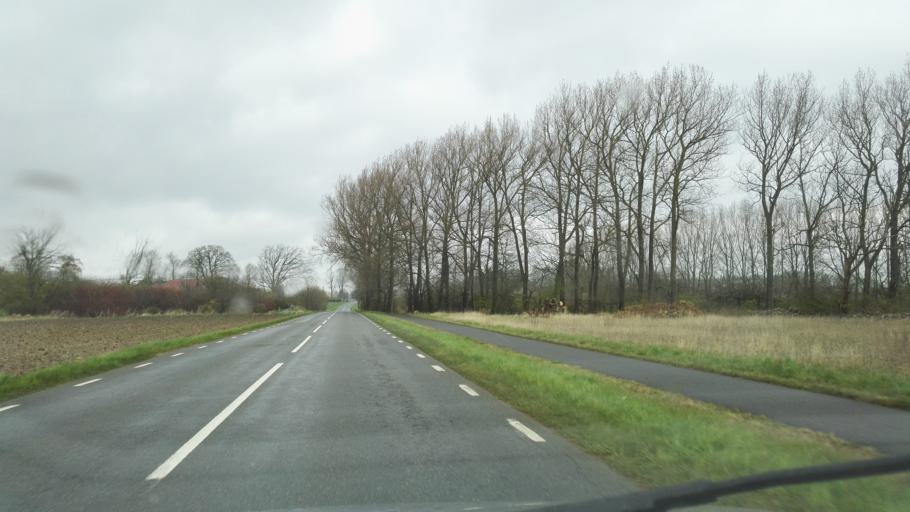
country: SE
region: Skane
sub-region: Simrishamns Kommun
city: Simrishamn
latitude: 55.4985
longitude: 14.3191
